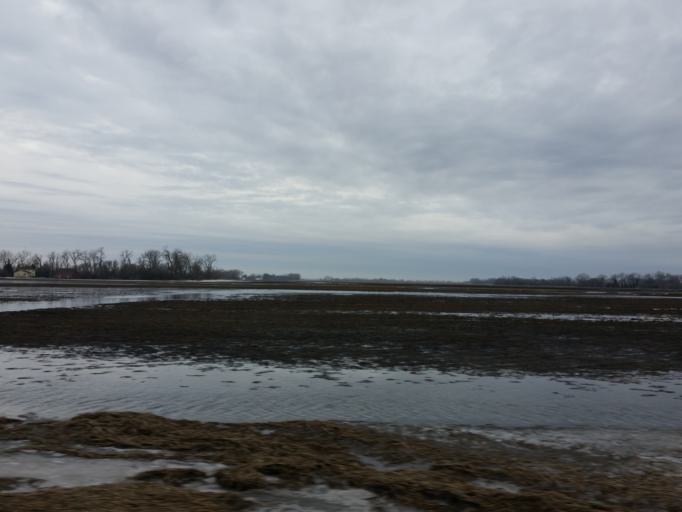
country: US
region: North Dakota
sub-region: Walsh County
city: Grafton
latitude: 48.3866
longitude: -97.4704
